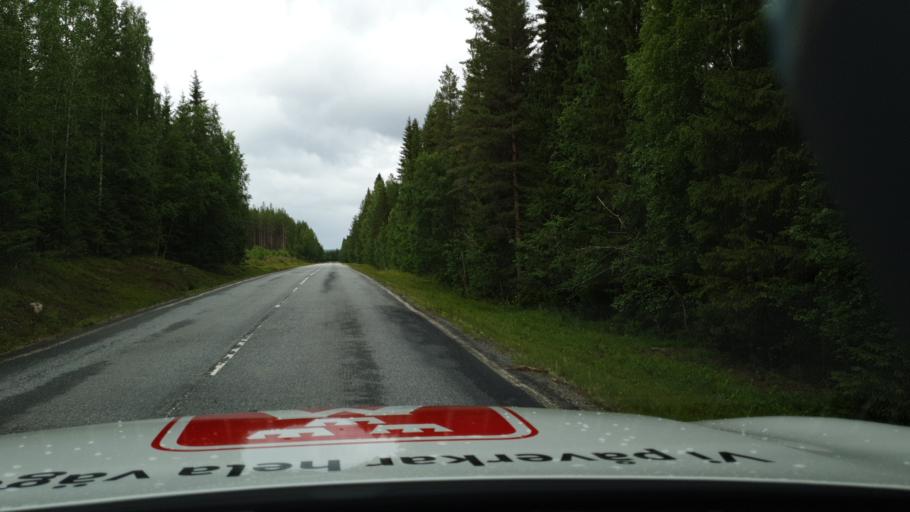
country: SE
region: Vaesterbotten
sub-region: Dorotea Kommun
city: Dorotea
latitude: 63.8740
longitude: 16.3759
